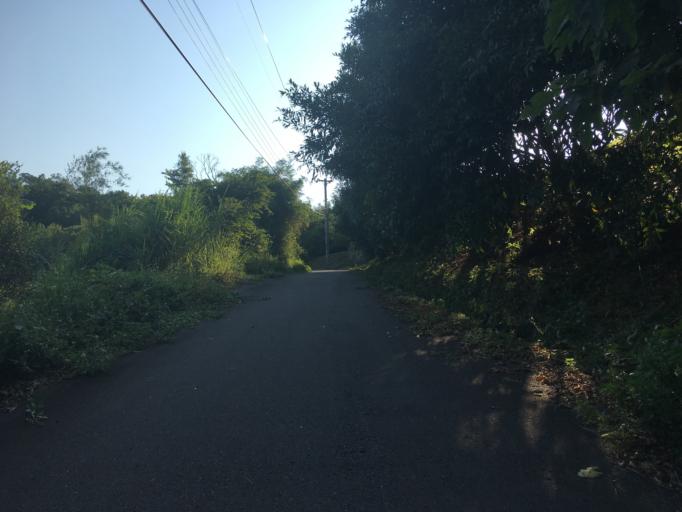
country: TW
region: Taiwan
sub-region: Hsinchu
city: Hsinchu
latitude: 24.7394
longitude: 120.9890
